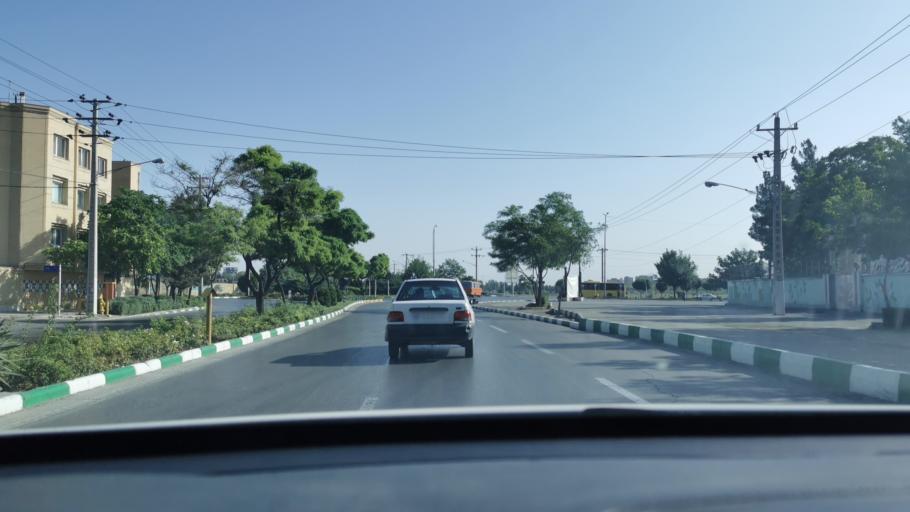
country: IR
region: Razavi Khorasan
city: Mashhad
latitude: 36.3401
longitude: 59.5076
